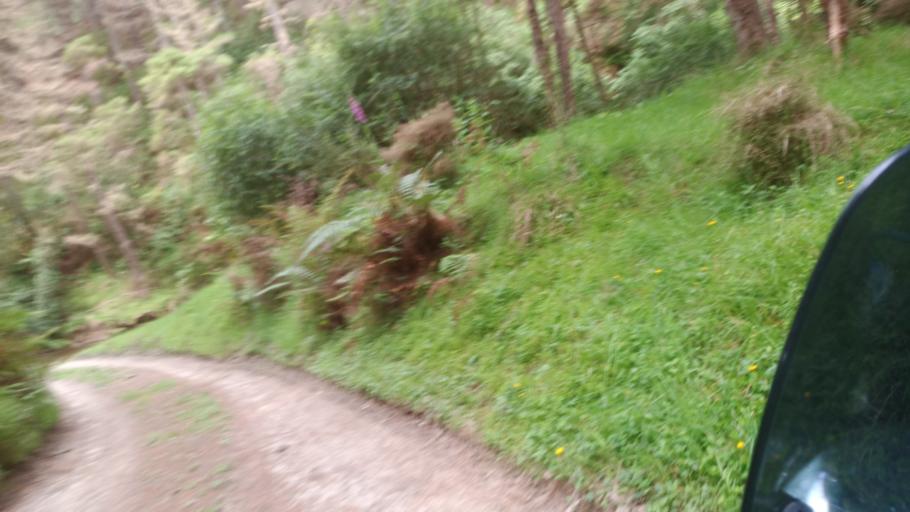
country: NZ
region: Gisborne
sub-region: Gisborne District
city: Gisborne
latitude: -38.4574
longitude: 177.9265
